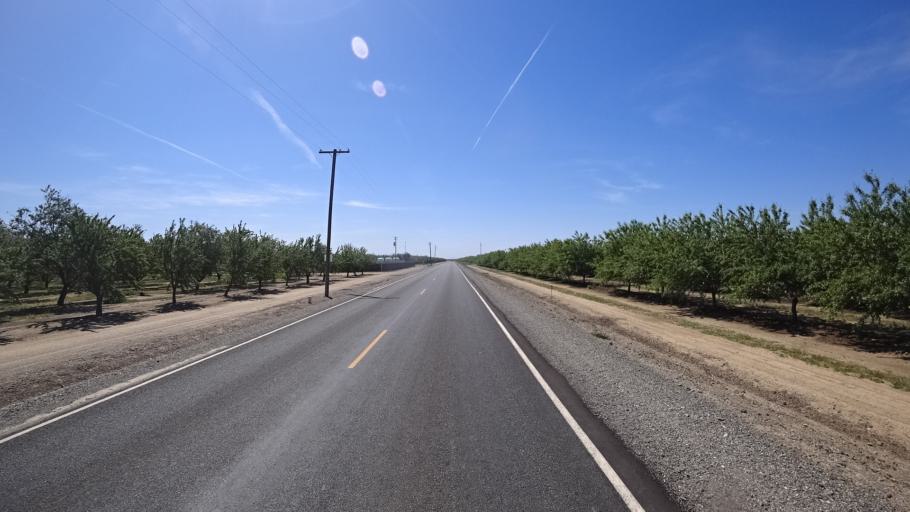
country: US
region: California
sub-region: Glenn County
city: Willows
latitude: 39.6324
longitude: -122.1413
